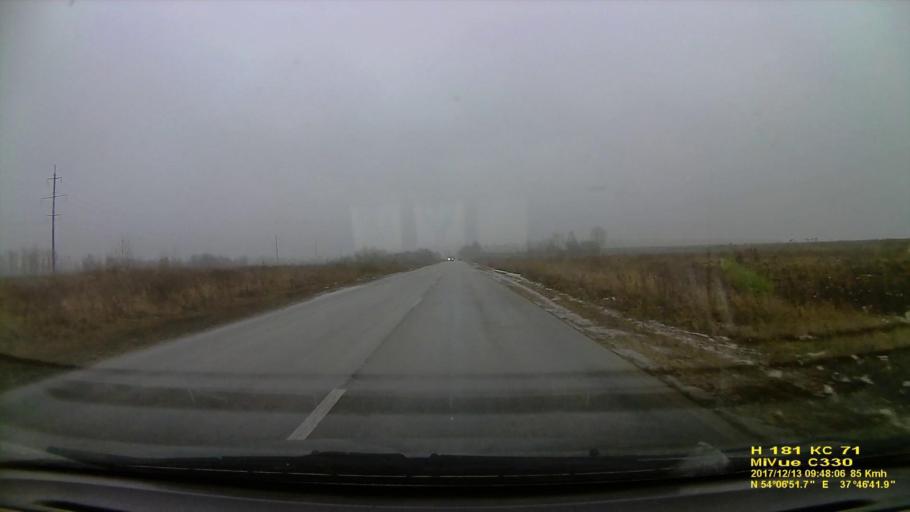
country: RU
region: Tula
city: Bolokhovo
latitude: 54.1144
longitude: 37.7783
